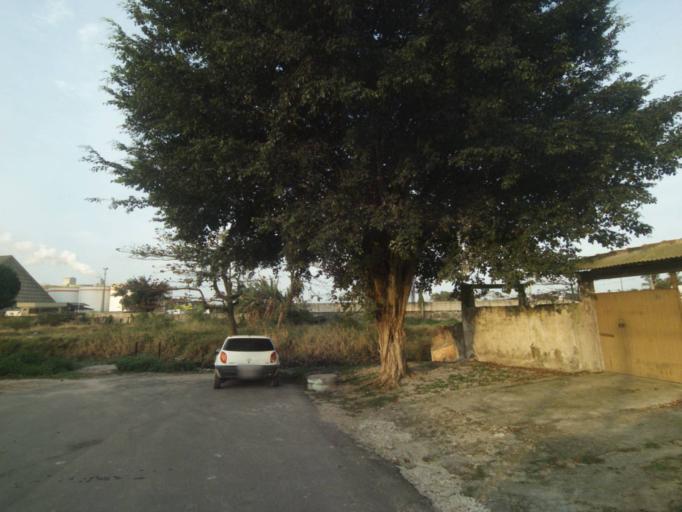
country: BR
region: Parana
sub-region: Paranagua
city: Paranagua
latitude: -25.5124
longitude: -48.5406
